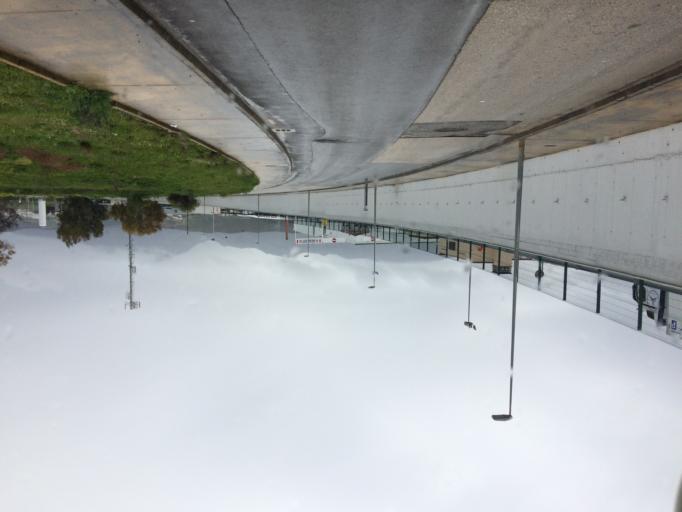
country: ES
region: Andalusia
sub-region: Provincia de Malaga
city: Antequera
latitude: 37.0399
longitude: -4.5288
